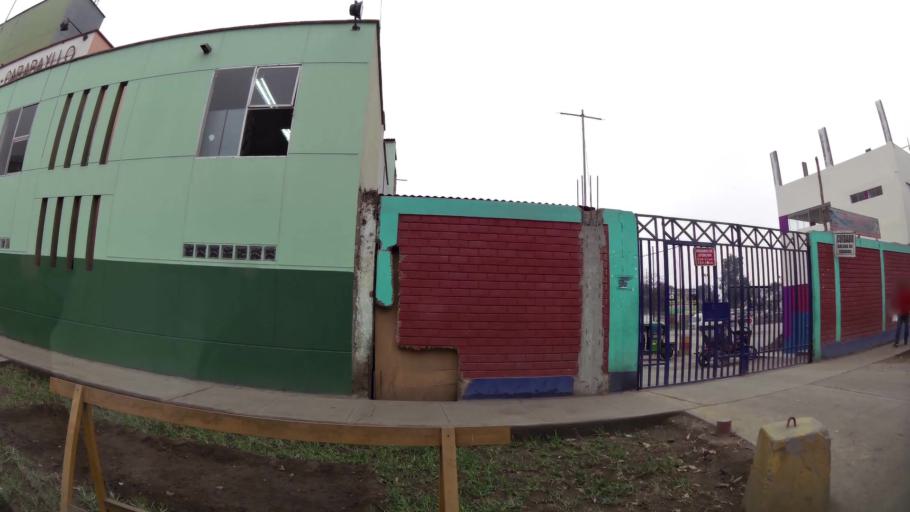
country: PE
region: Lima
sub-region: Lima
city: Urb. Santo Domingo
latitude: -11.9015
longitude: -77.0324
